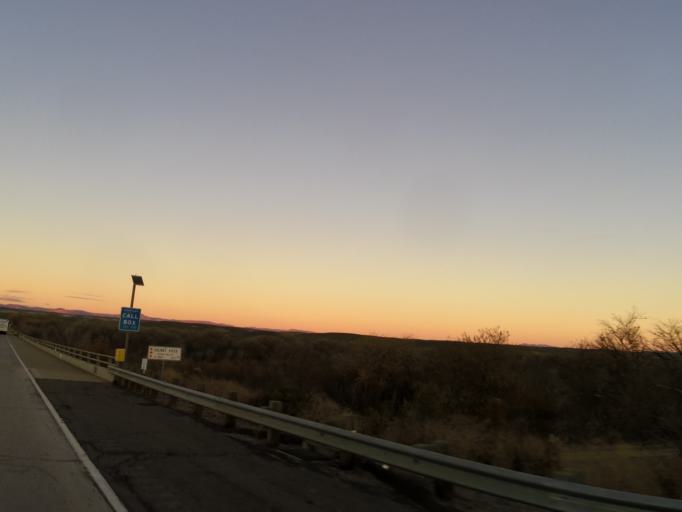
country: US
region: California
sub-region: Monterey County
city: King City
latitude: 36.1055
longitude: -121.0236
